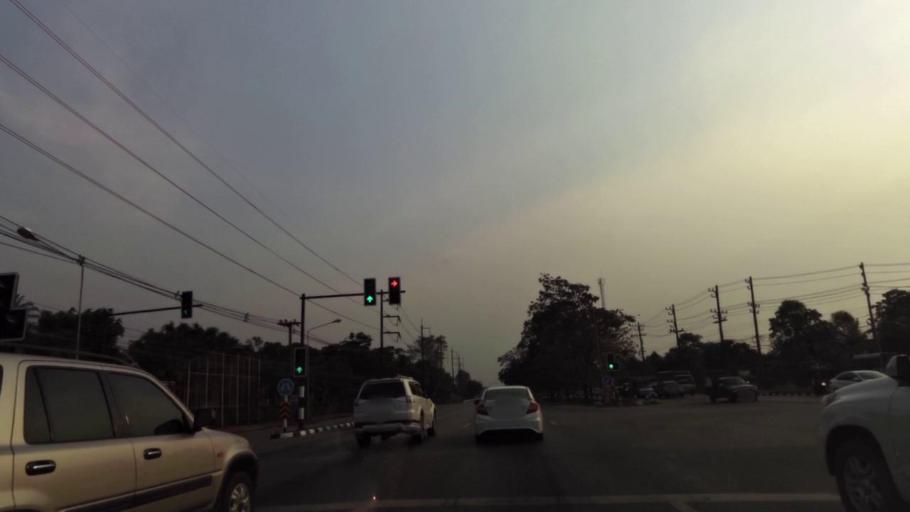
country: TH
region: Chanthaburi
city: Khlung
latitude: 12.5111
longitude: 102.1691
